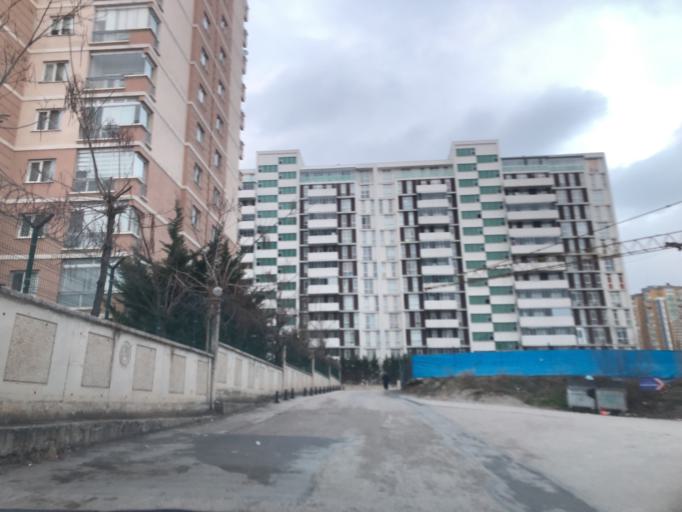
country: TR
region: Ankara
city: Batikent
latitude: 39.9641
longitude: 32.7727
